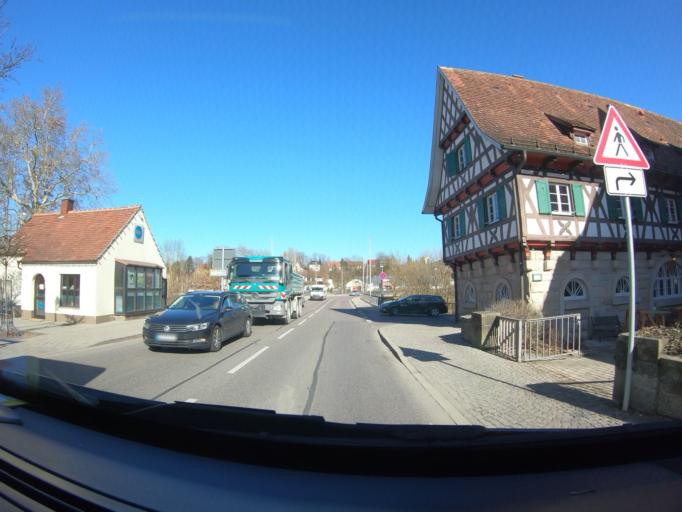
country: DE
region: Baden-Wuerttemberg
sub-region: Regierungsbezirk Stuttgart
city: Gaildorf
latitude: 49.0016
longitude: 9.7704
